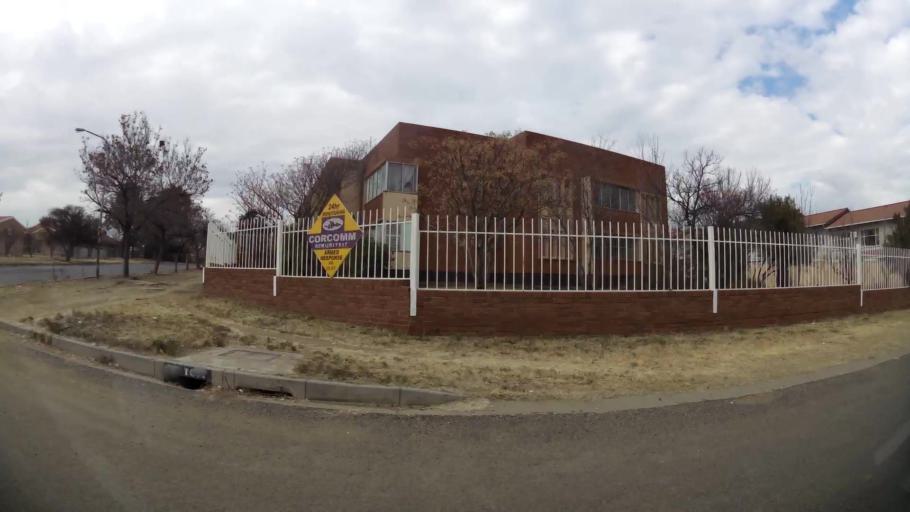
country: ZA
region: Orange Free State
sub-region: Fezile Dabi District Municipality
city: Kroonstad
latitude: -27.6473
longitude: 27.2324
